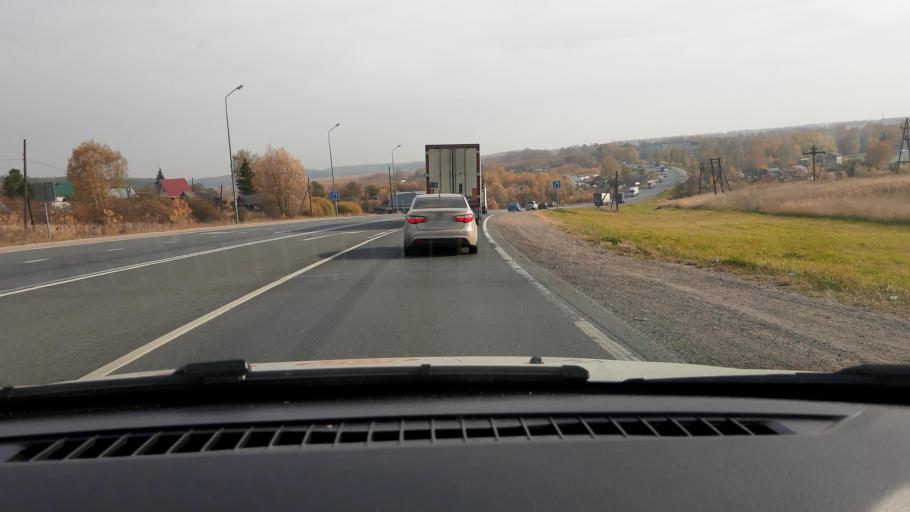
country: RU
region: Nizjnij Novgorod
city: Pamyat' Parizhskoy Kommuny
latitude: 56.0455
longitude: 44.4340
